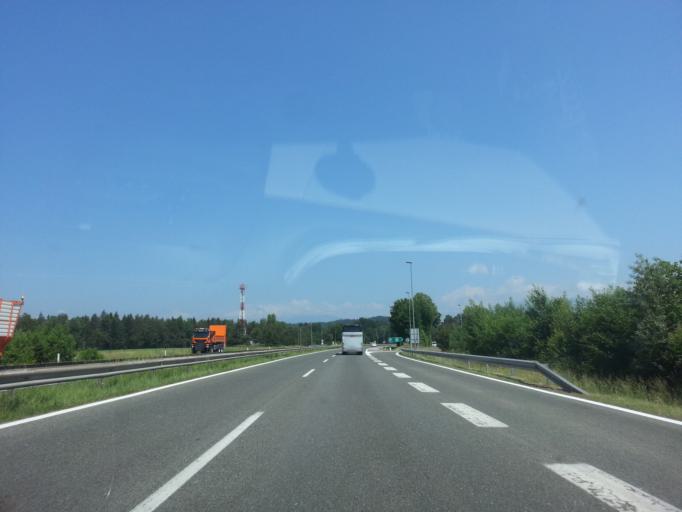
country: SI
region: Medvode
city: Zgornje Pirnice
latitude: 46.1422
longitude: 14.4764
